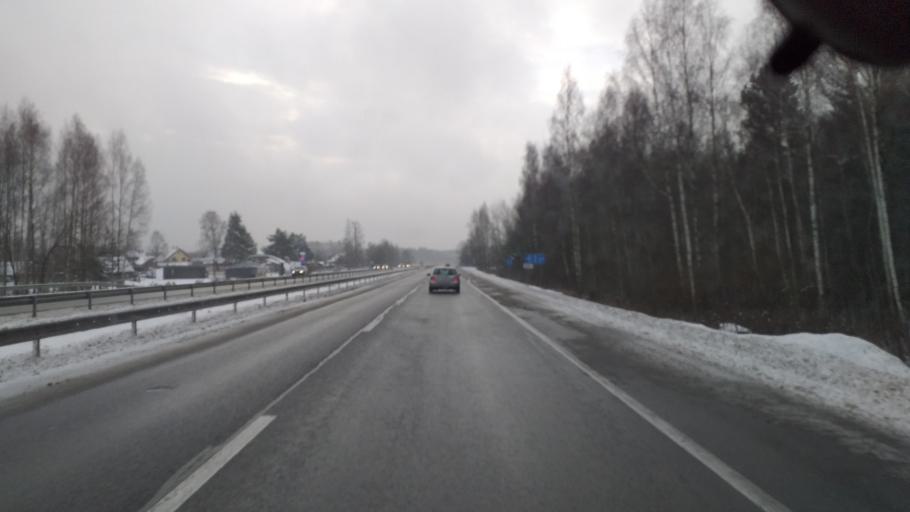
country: LV
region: Marupe
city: Marupe
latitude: 56.8593
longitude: 24.0642
